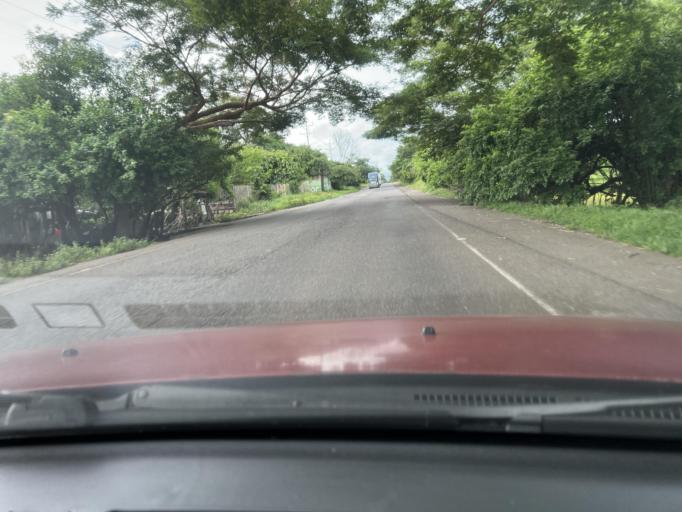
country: SV
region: La Union
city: San Alejo
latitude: 13.4122
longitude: -87.8901
